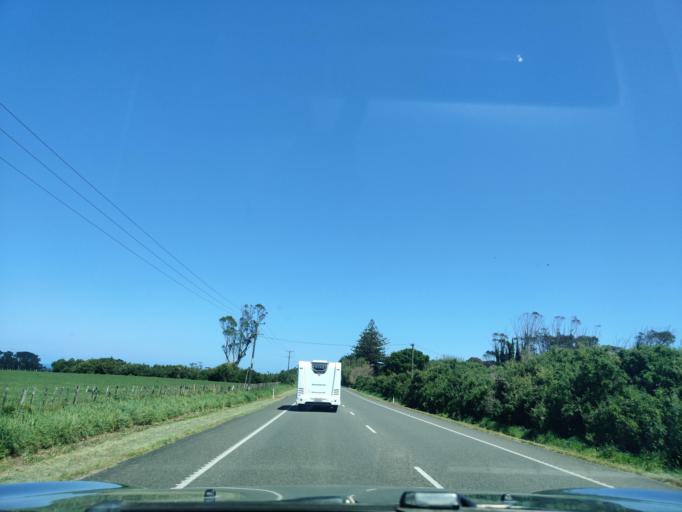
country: NZ
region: Taranaki
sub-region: South Taranaki District
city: Patea
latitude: -39.8079
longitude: 174.7559
